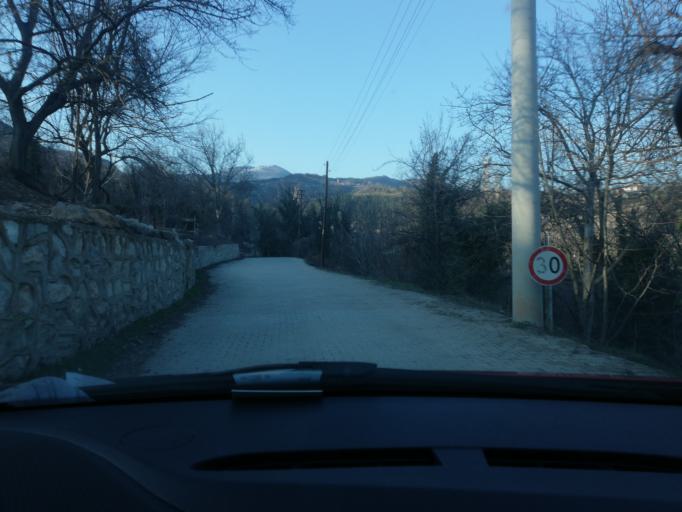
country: TR
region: Karabuk
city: Safranbolu
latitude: 41.2835
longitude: 32.6785
